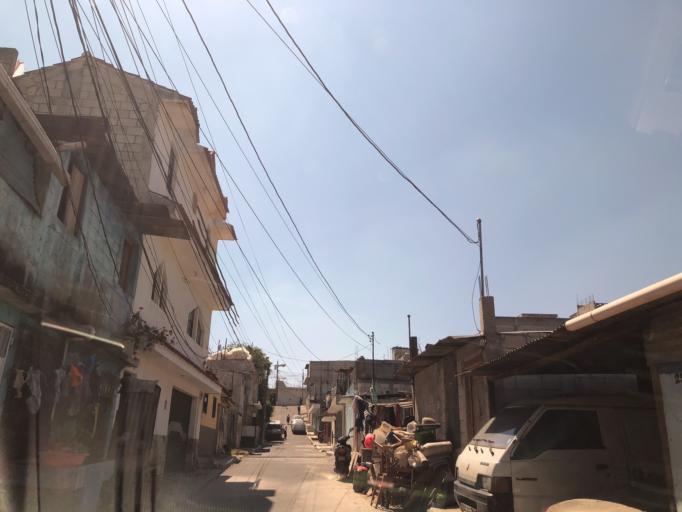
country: GT
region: Guatemala
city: Mixco
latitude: 14.6228
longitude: -90.5808
